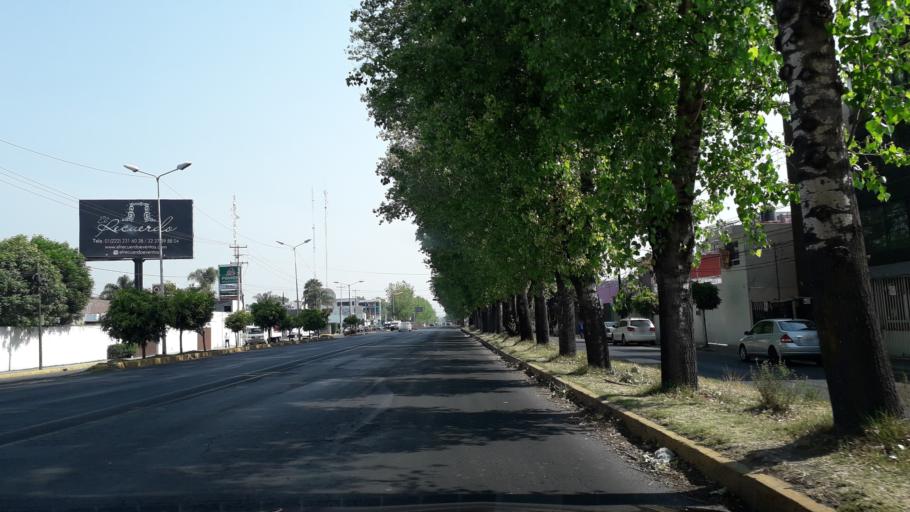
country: MX
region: Puebla
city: Puebla
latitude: 19.0718
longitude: -98.2190
